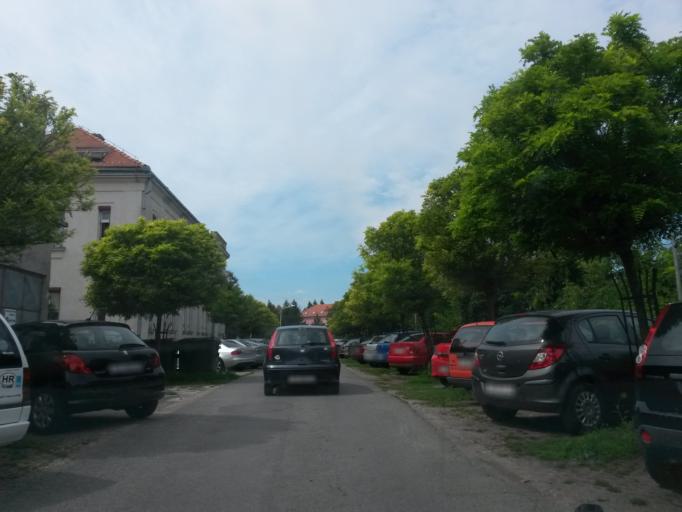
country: HR
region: Osjecko-Baranjska
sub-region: Grad Osijek
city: Osijek
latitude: 45.5581
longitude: 18.7098
